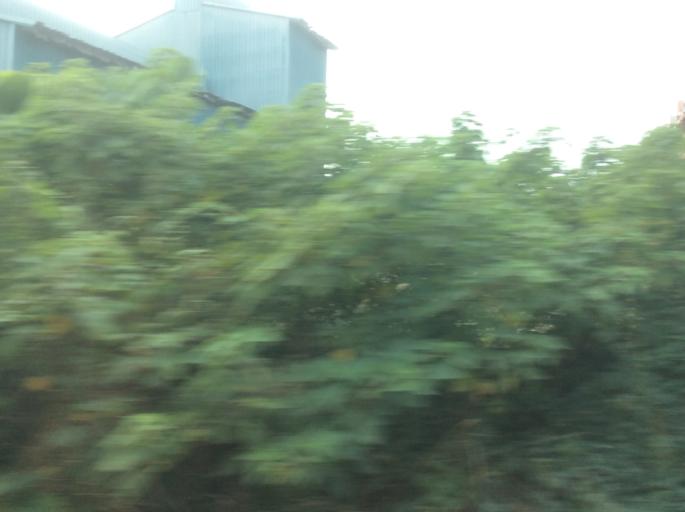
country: TW
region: Taiwan
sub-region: Chiayi
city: Jiayi Shi
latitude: 23.5193
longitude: 120.4395
